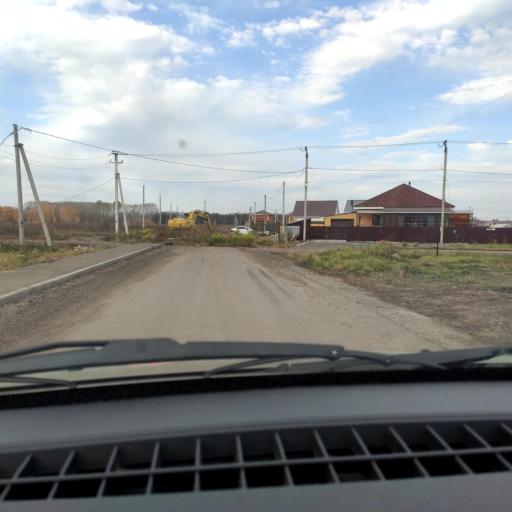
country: RU
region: Bashkortostan
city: Ufa
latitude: 54.6284
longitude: 55.9045
